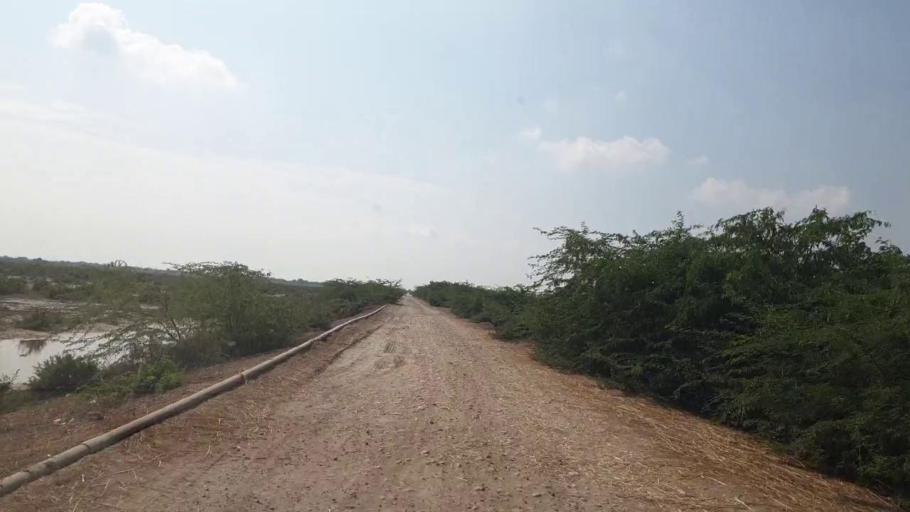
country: PK
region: Sindh
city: Badin
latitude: 24.5000
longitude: 68.6070
